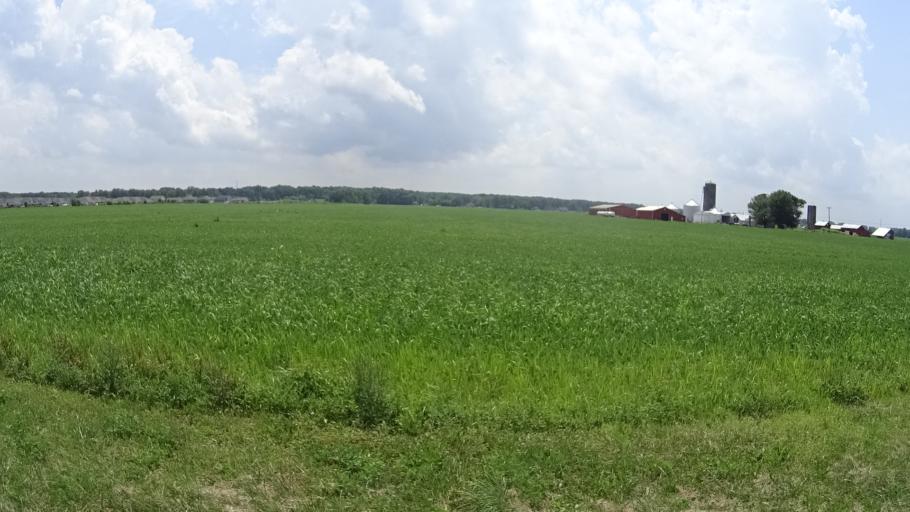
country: US
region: Ohio
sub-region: Lorain County
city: Vermilion
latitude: 41.4102
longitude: -82.3750
